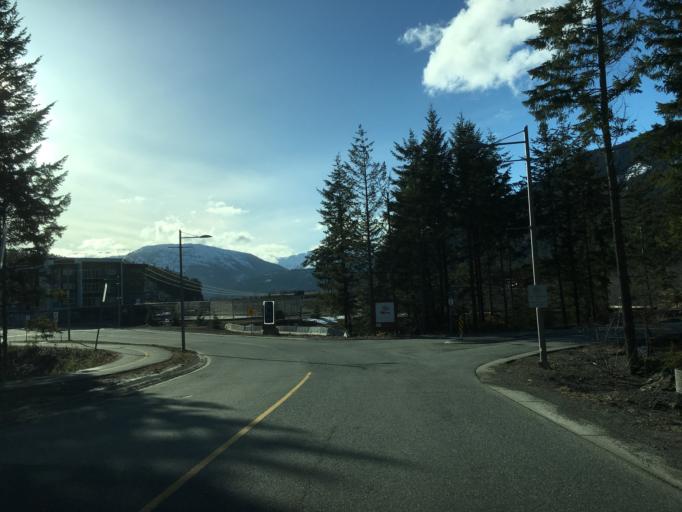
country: CA
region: British Columbia
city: Whistler
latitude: 50.0812
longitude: -123.0389
